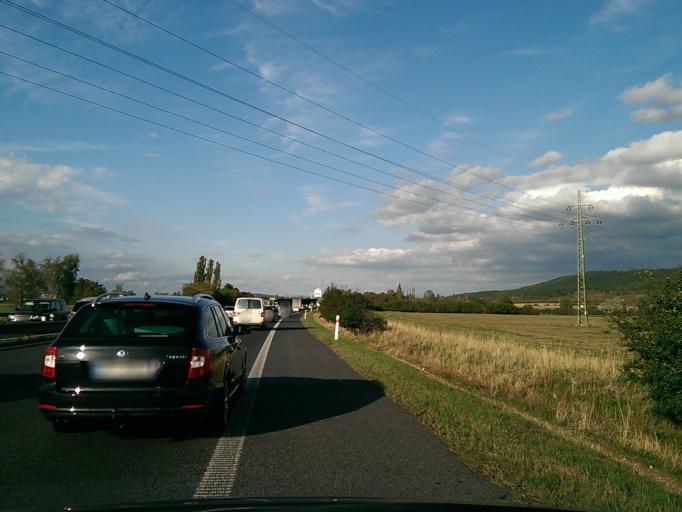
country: CZ
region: Central Bohemia
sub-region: Okres Mlada Boleslav
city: Mlada Boleslav
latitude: 50.3785
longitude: 14.8898
